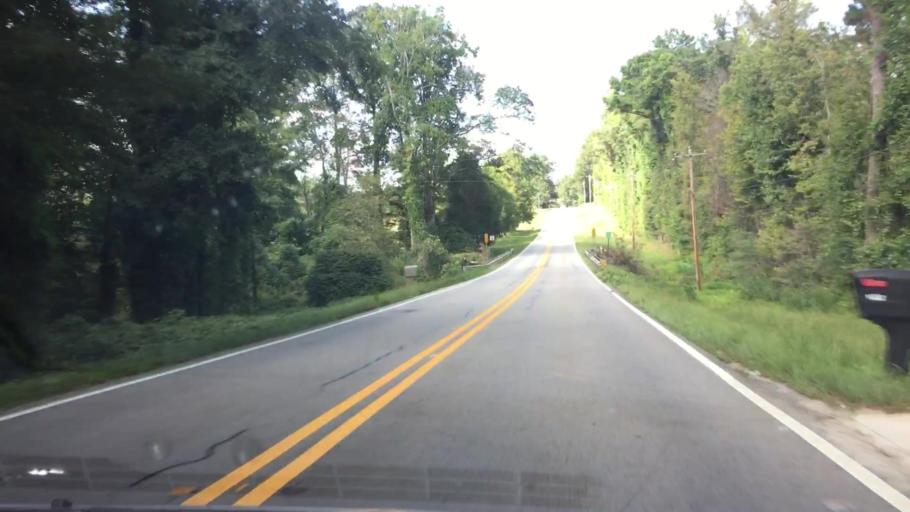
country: US
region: Georgia
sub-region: Fayette County
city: Shannon
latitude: 33.4005
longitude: -84.4946
